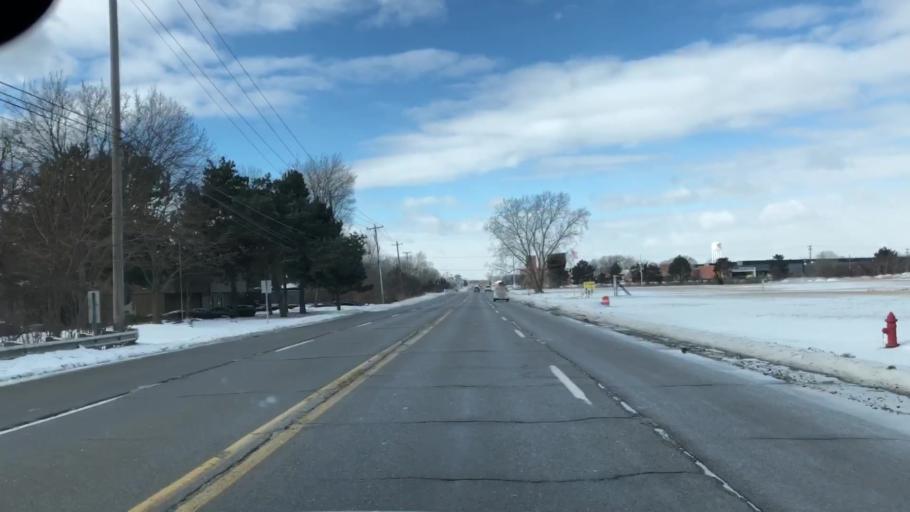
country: US
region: Michigan
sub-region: Wayne County
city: Plymouth
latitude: 42.3723
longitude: -83.4332
